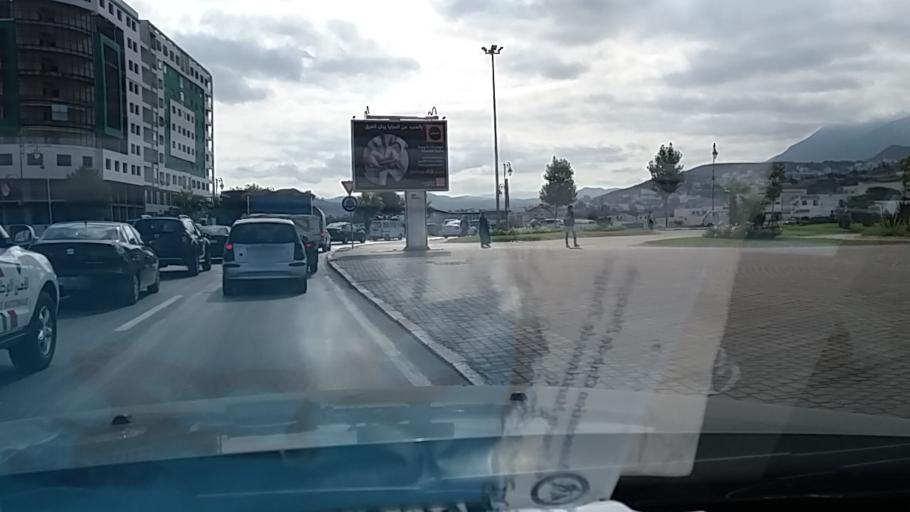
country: MA
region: Tanger-Tetouan
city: Tetouan
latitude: 35.5613
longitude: -5.3710
